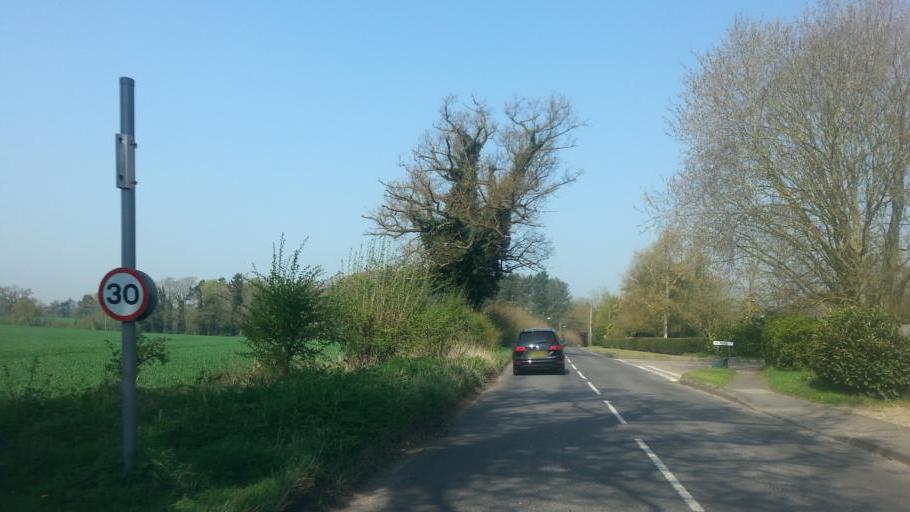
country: GB
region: England
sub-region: Suffolk
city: Thurston
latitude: 52.2478
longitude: 0.8124
